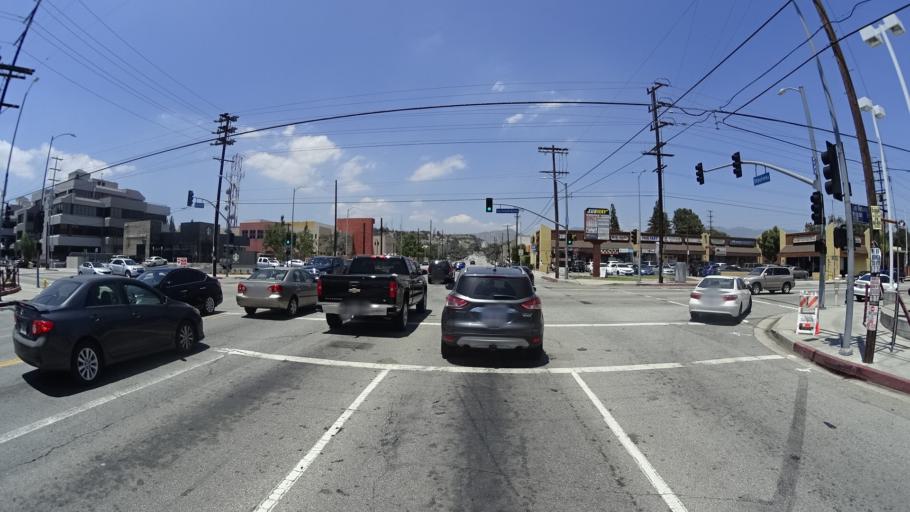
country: US
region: California
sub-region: Los Angeles County
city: San Fernando
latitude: 34.2719
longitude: -118.4674
